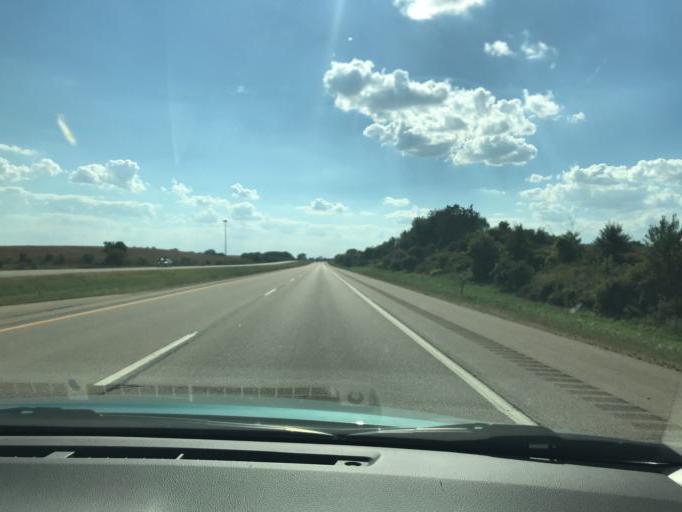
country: US
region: Wisconsin
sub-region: Rock County
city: Clinton
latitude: 42.5593
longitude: -88.9171
